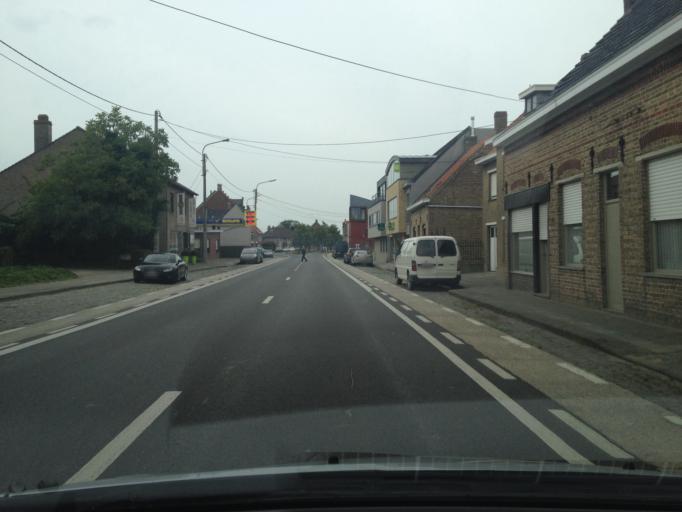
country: BE
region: Flanders
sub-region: Provincie West-Vlaanderen
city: Diksmuide
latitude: 50.9996
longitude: 2.8697
